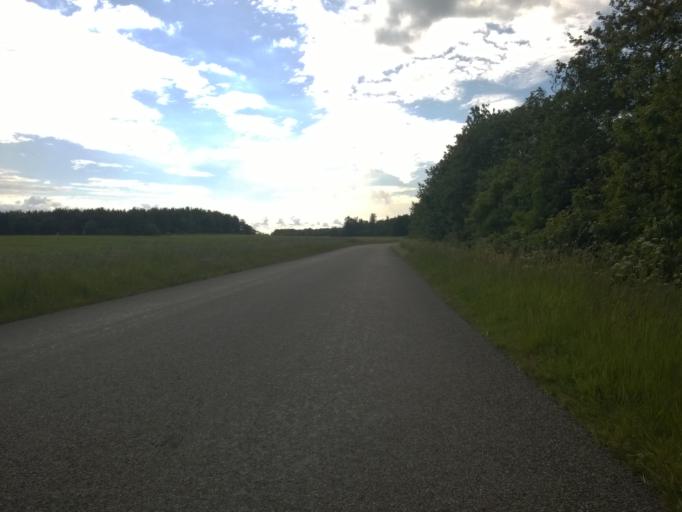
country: DK
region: Central Jutland
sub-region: Holstebro Kommune
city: Vinderup
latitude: 56.4817
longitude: 8.8501
